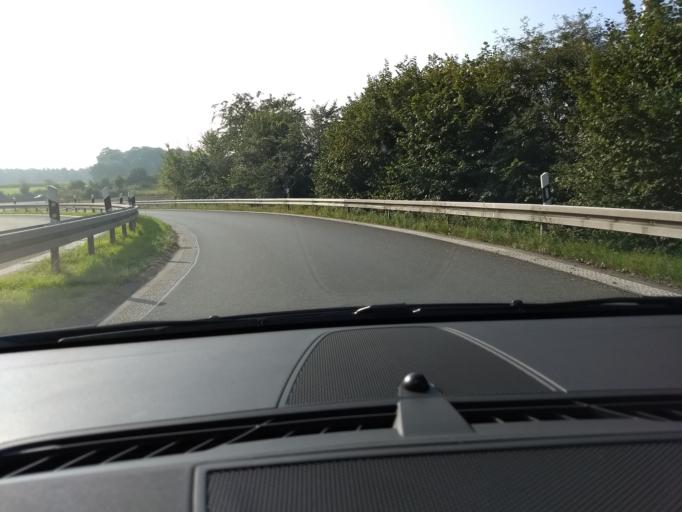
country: DE
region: North Rhine-Westphalia
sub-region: Regierungsbezirk Munster
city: Heiden
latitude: 51.8073
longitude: 6.9816
